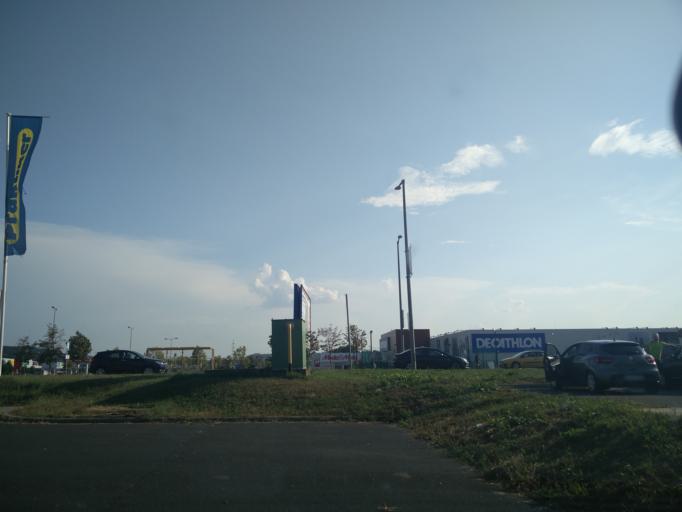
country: HU
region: Zala
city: Zalaegerszeg
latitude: 46.8441
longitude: 16.8675
